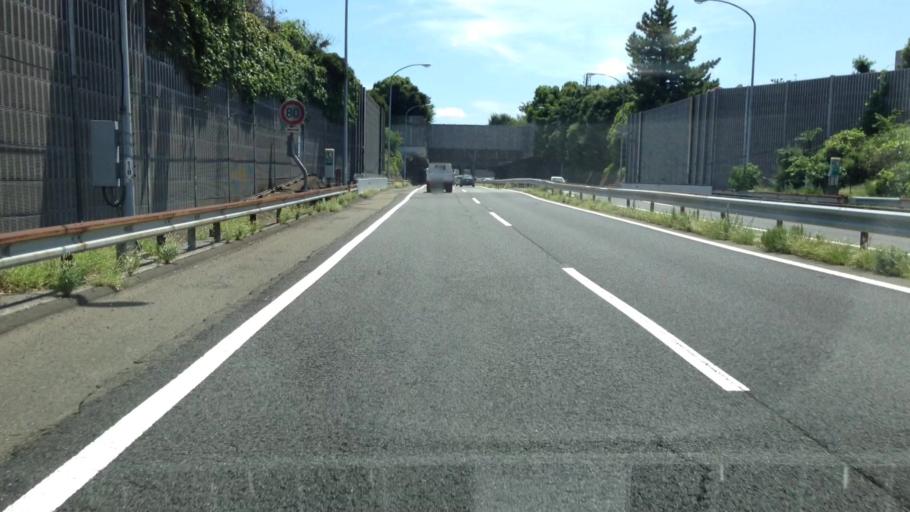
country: JP
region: Kanagawa
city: Yokohama
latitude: 35.4060
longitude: 139.5752
